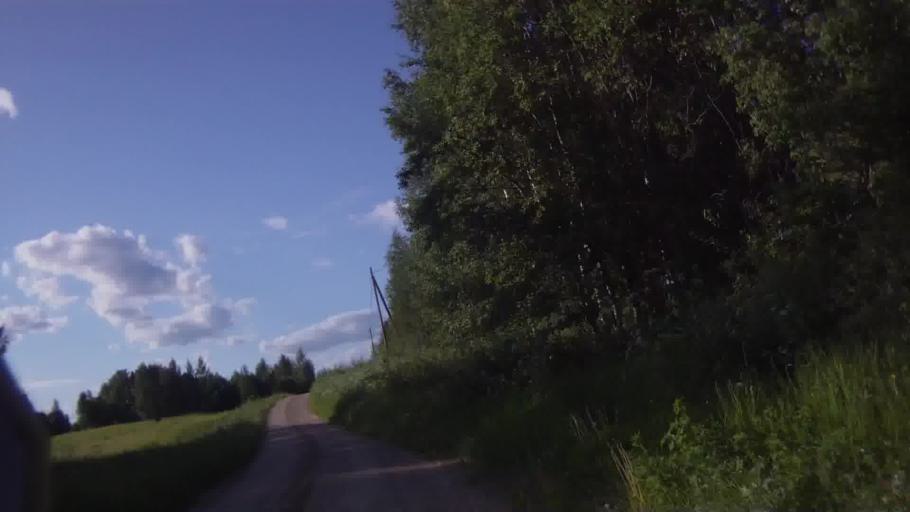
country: LV
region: Dagda
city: Dagda
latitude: 56.2758
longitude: 27.4693
